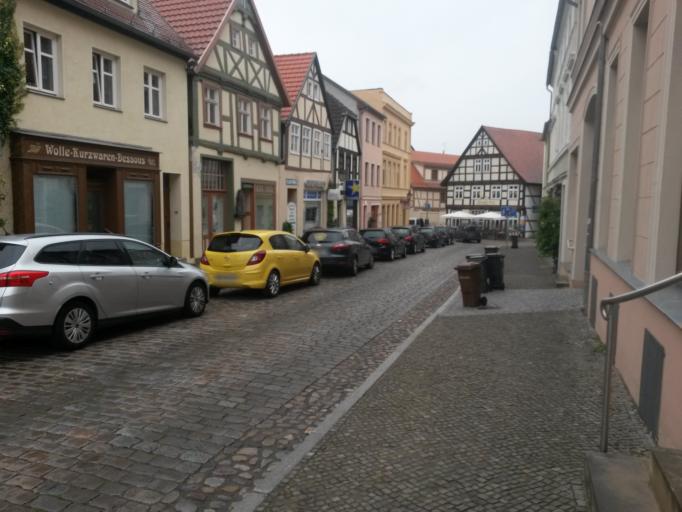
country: DE
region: Saxony-Anhalt
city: Havelberg
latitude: 52.8255
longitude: 12.0744
